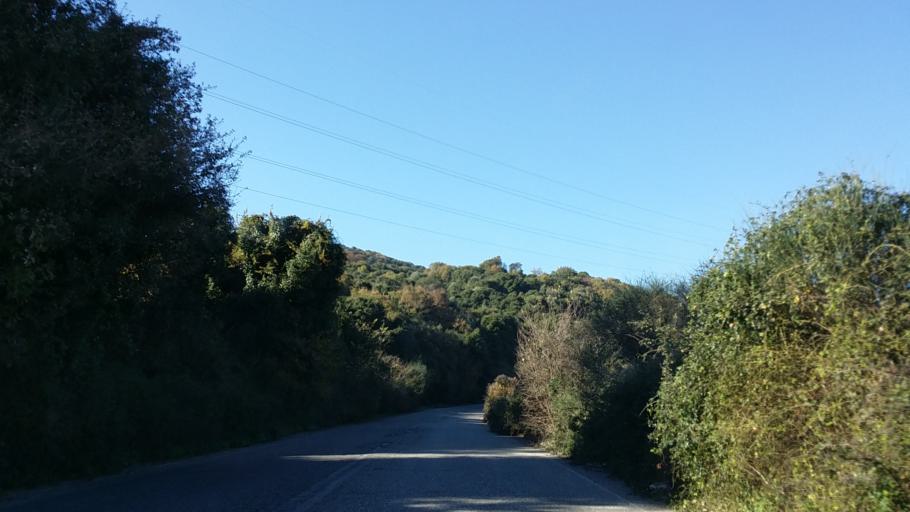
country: GR
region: West Greece
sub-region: Nomos Aitolias kai Akarnanias
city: Monastirakion
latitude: 38.8715
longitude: 21.0456
